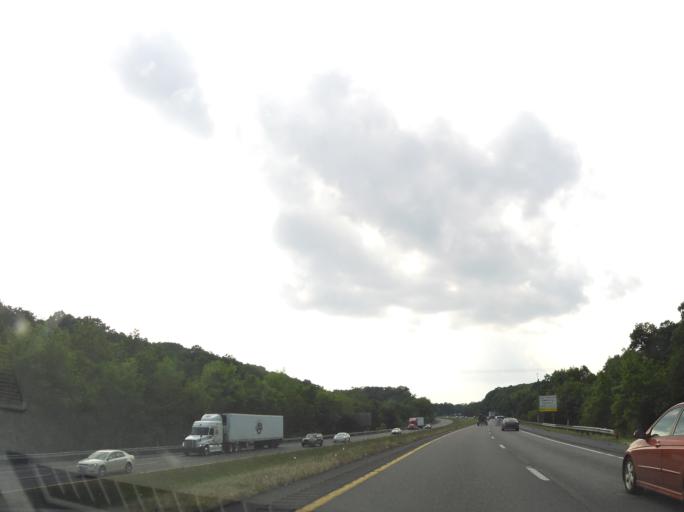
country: US
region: Maryland
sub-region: Washington County
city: Williamsport
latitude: 39.5848
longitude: -77.8365
